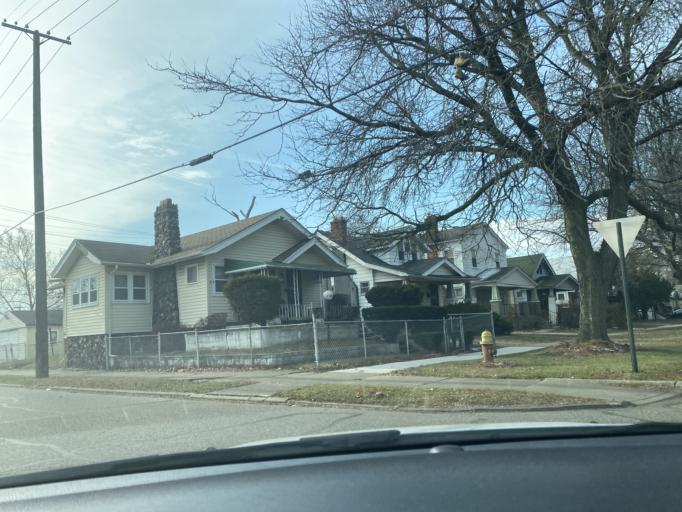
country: US
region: Michigan
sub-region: Wayne County
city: Highland Park
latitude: 42.3743
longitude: -83.1415
